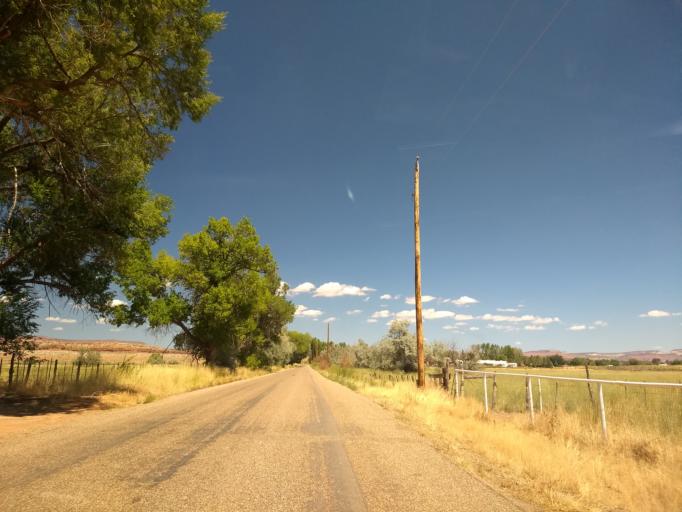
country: US
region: Arizona
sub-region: Coconino County
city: Fredonia
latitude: 36.9380
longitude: -112.5353
